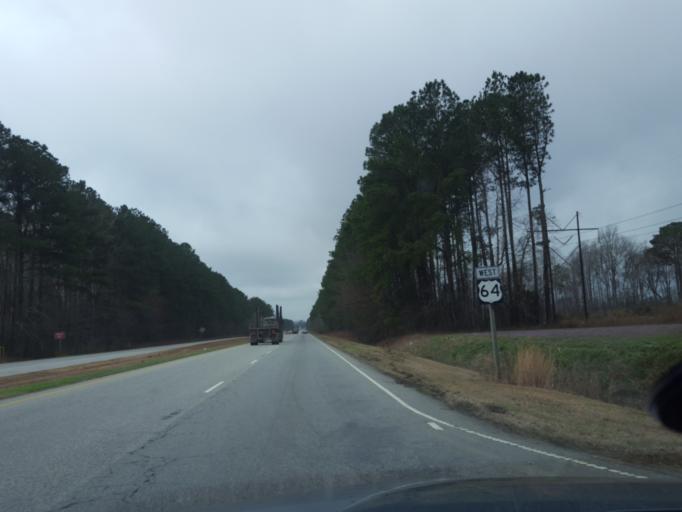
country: US
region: North Carolina
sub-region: Washington County
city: Plymouth
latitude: 35.8271
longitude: -76.8202
